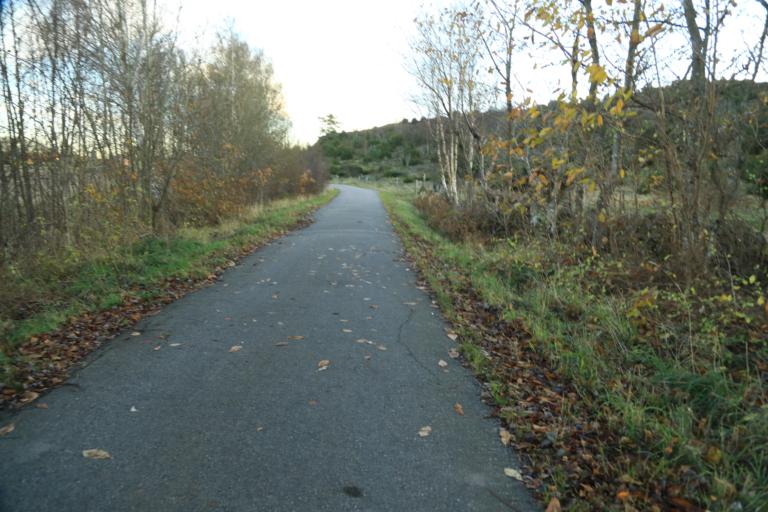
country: SE
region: Halland
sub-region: Varbergs Kommun
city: Varberg
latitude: 57.1621
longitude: 12.2383
